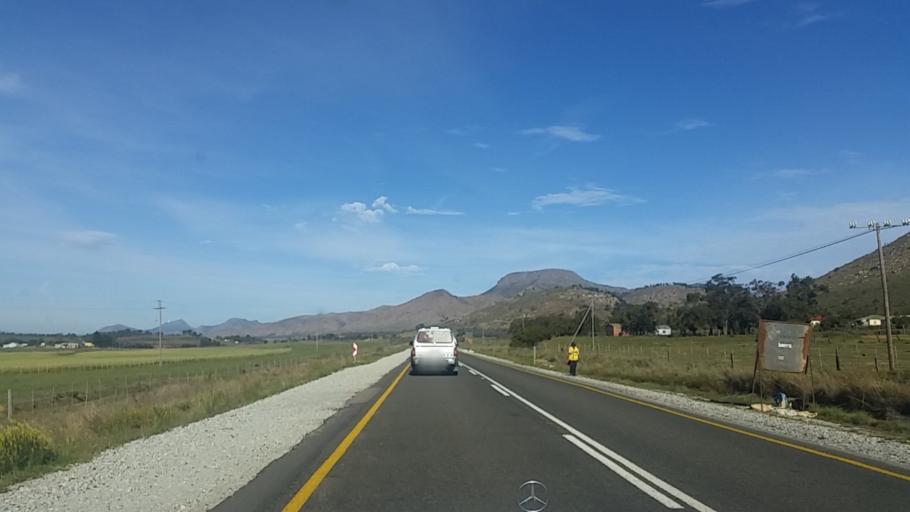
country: ZA
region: Western Cape
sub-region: Eden District Municipality
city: George
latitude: -33.8309
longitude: 22.4299
